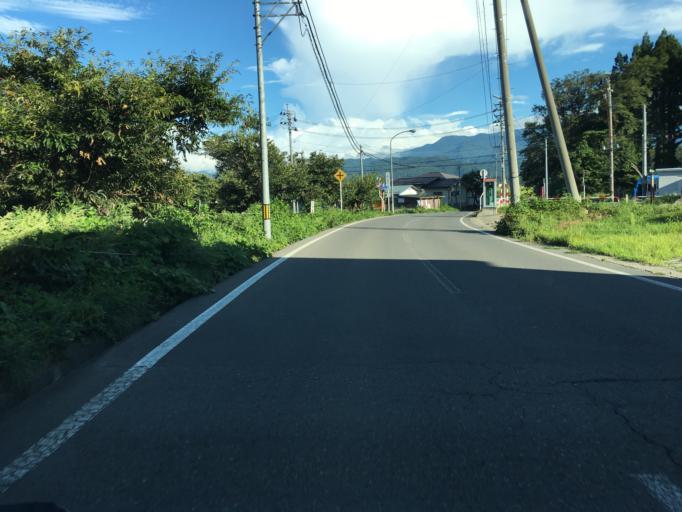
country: JP
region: Yamagata
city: Yonezawa
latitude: 37.8915
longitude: 140.0930
